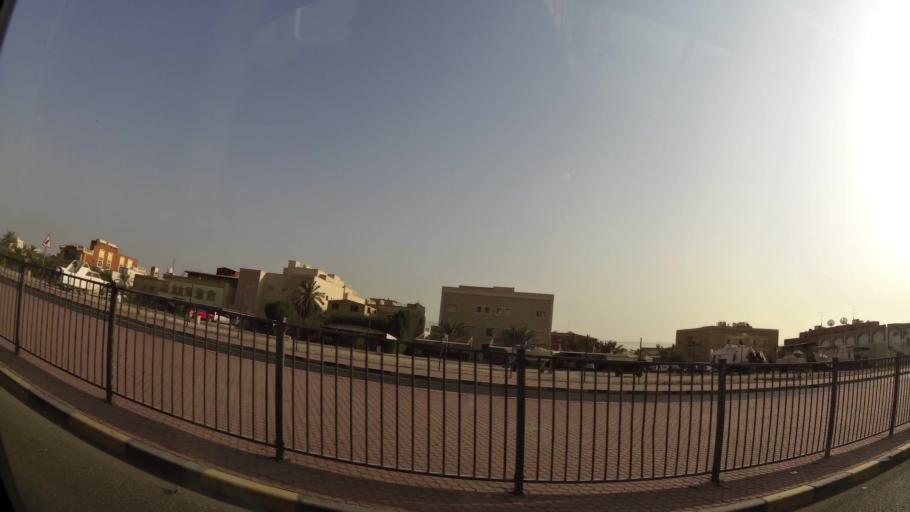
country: KW
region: Muhafazat Hawalli
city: As Salimiyah
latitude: 29.3246
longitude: 48.0694
